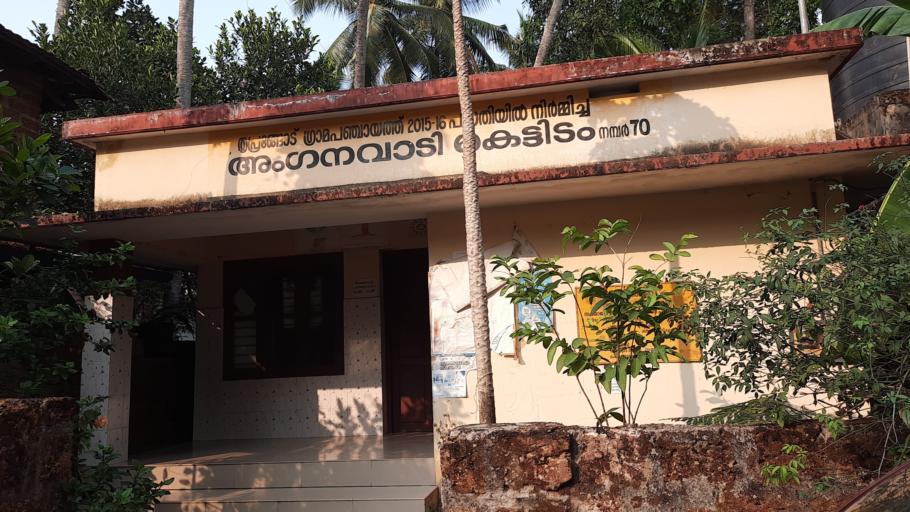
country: IN
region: Kerala
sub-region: Malappuram
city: Ponnani
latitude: 10.8171
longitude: 75.9534
